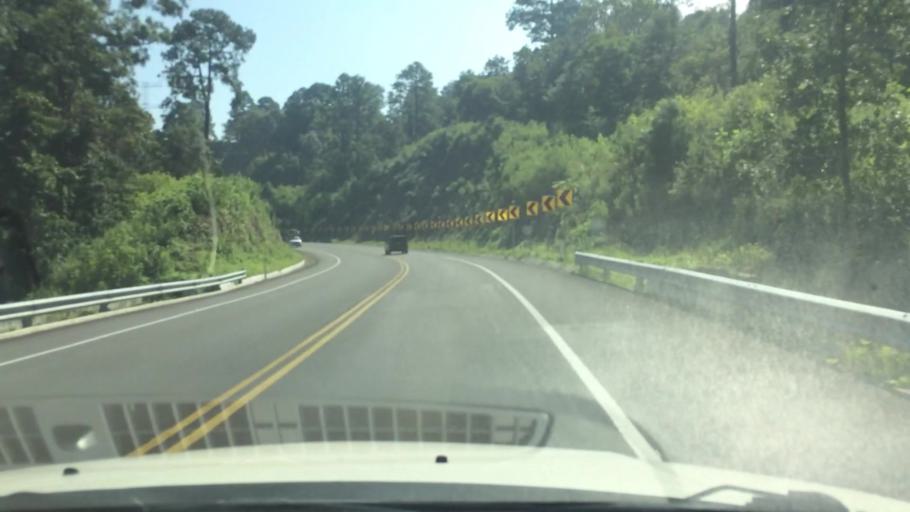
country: MX
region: Mexico
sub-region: Amanalco
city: Polvillos (San Bartolo Quinta Seccion)
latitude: 19.2197
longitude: -100.0905
